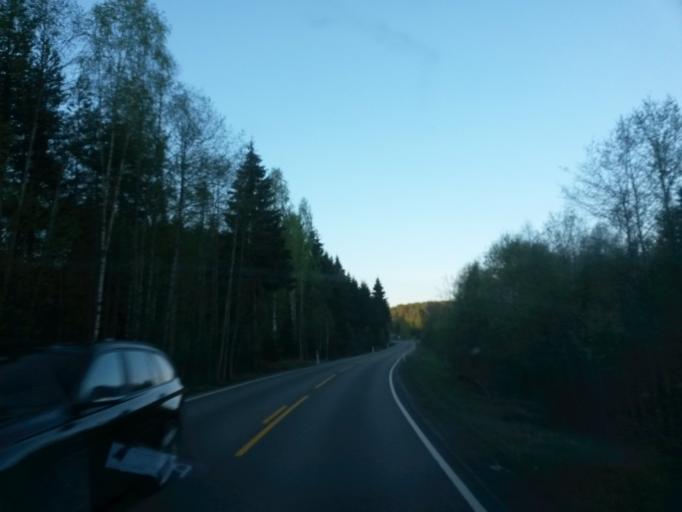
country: NO
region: Buskerud
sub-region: Kongsberg
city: Kongsberg
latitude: 59.6548
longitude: 9.7463
